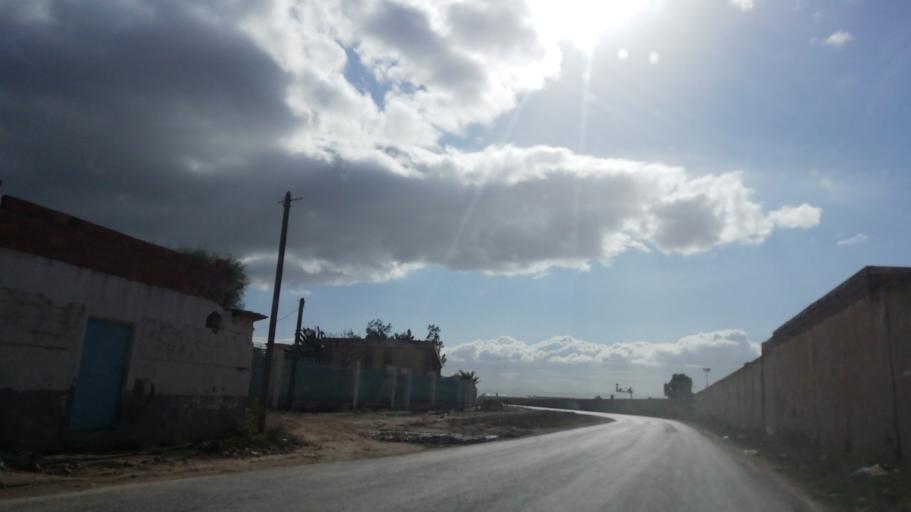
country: DZ
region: Oran
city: Es Senia
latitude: 35.6491
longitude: -0.6061
